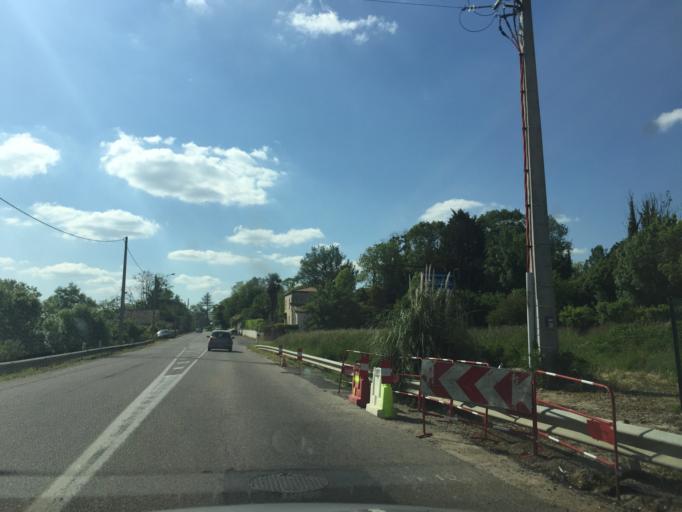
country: FR
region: Aquitaine
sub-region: Departement de la Gironde
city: La Reole
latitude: 44.5788
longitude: -0.0202
